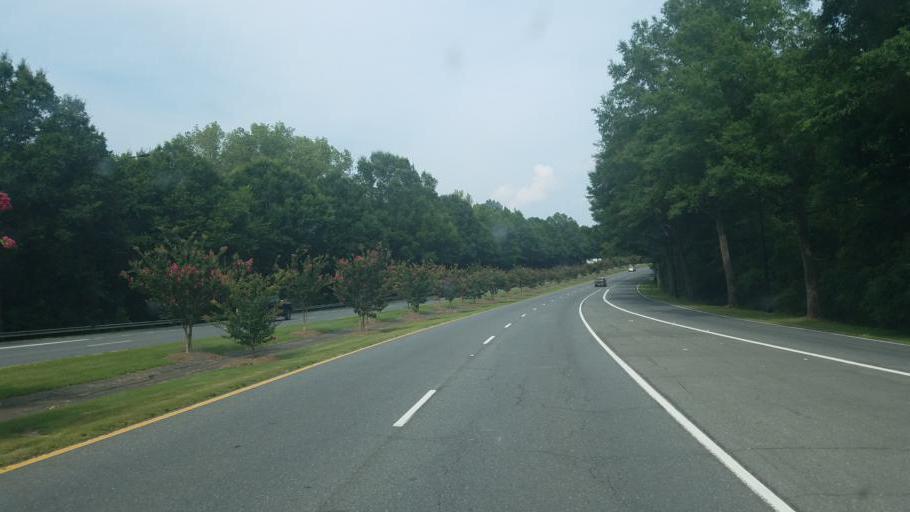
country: US
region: South Carolina
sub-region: York County
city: Rock Hill
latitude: 34.9403
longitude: -80.9949
